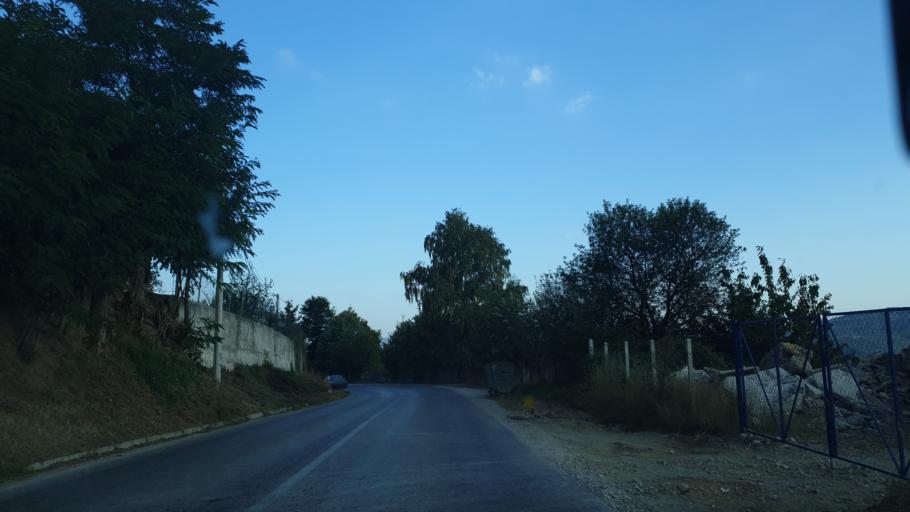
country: RS
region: Central Serbia
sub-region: Zlatiborski Okrug
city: Uzice
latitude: 43.8619
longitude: 19.8837
